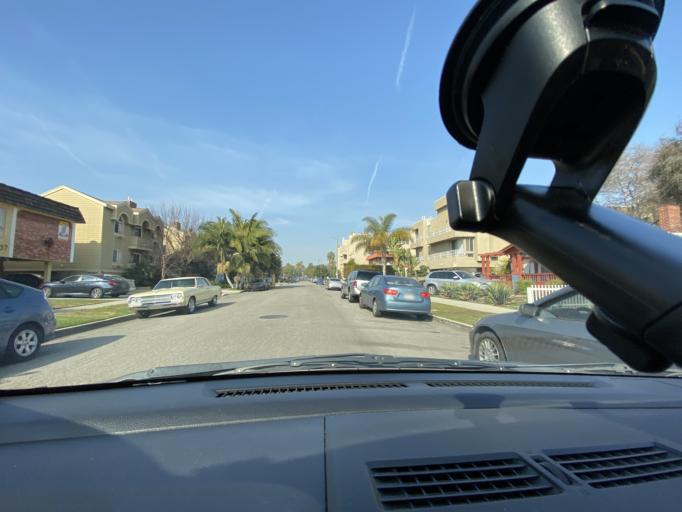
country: US
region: California
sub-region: Los Angeles County
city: Culver City
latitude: 34.0246
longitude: -118.4041
